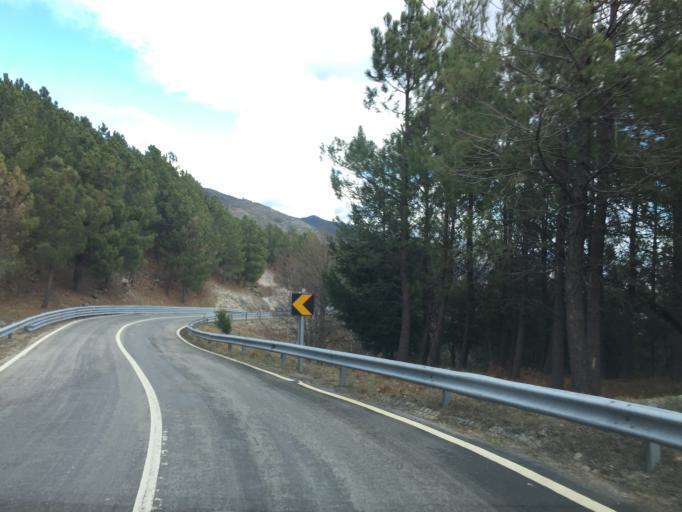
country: PT
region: Castelo Branco
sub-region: Covilha
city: Covilha
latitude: 40.2837
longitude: -7.5218
